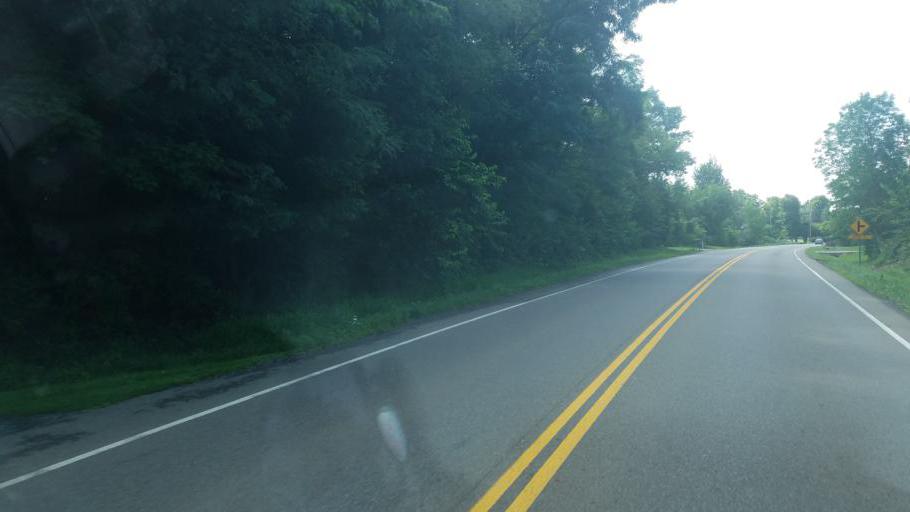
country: US
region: Ohio
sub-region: Licking County
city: Granville South
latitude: 40.0115
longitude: -82.5227
